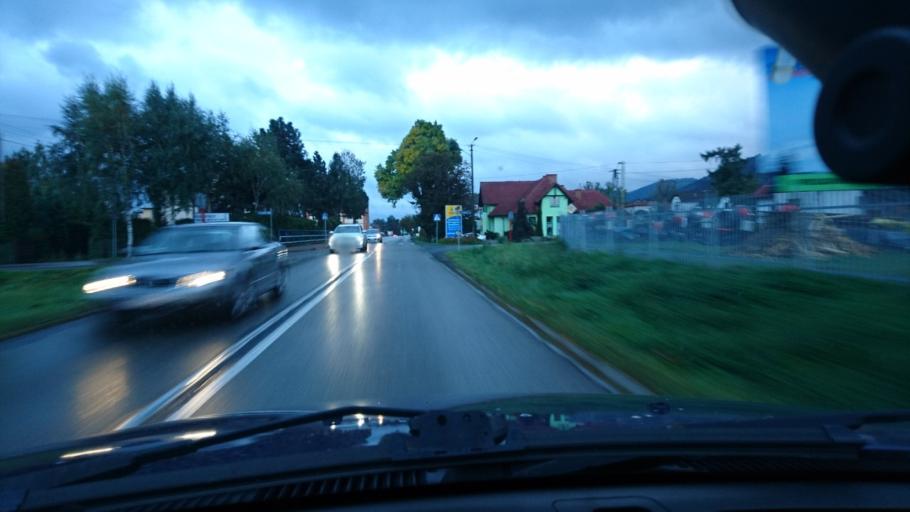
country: PL
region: Silesian Voivodeship
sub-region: Powiat bielski
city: Buczkowice
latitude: 49.7319
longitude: 19.0678
